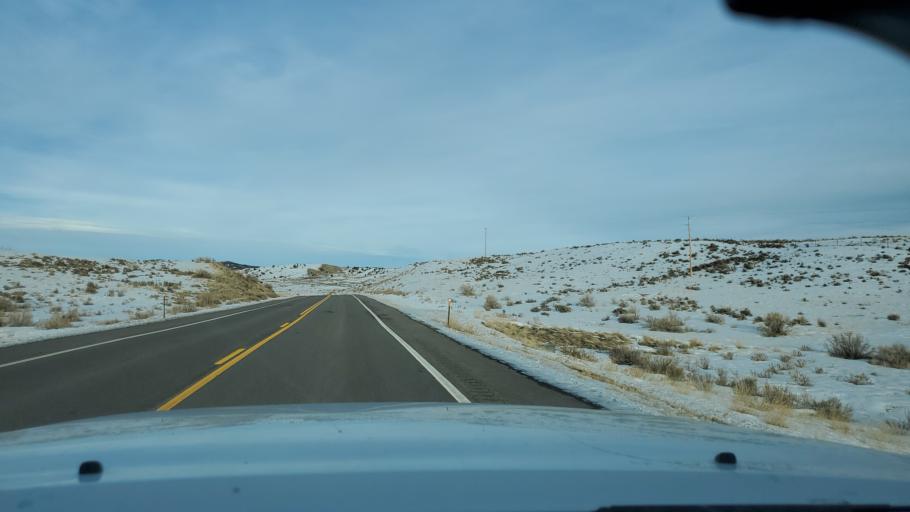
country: US
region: Colorado
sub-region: Rio Blanco County
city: Rangely
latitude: 40.3178
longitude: -108.5100
